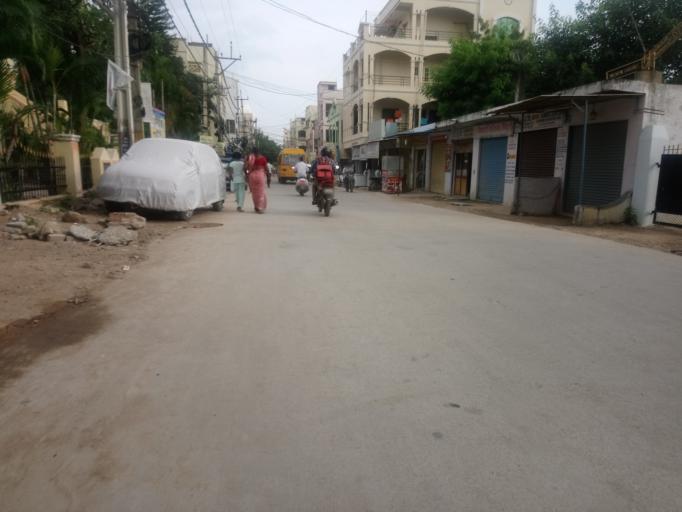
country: IN
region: Telangana
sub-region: Rangareddi
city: Kukatpalli
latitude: 17.5027
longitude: 78.4185
